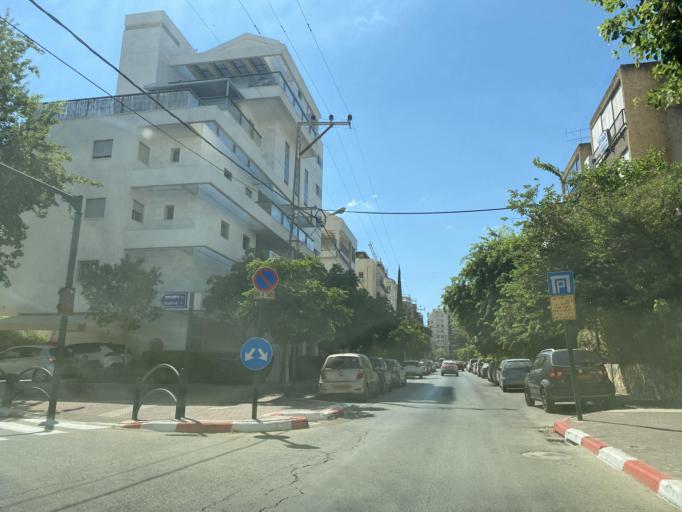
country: IL
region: Central District
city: Kfar Saba
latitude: 32.1732
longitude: 34.9048
